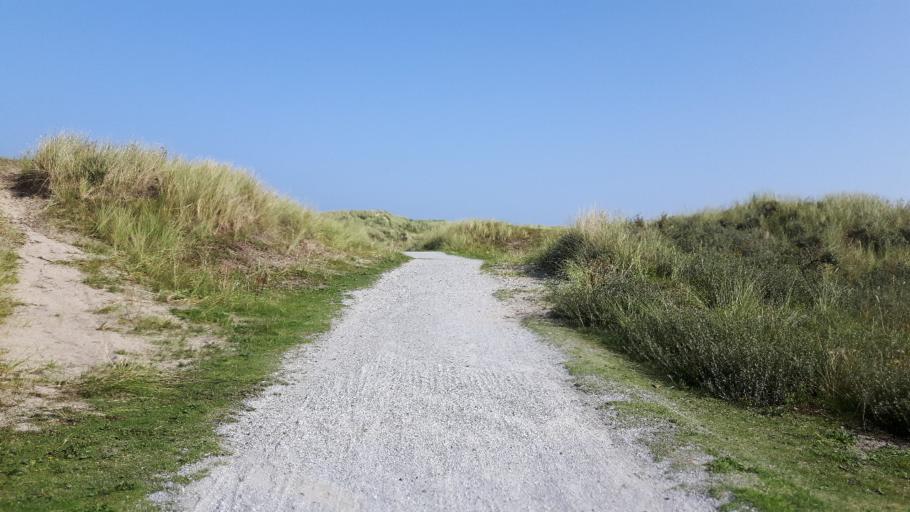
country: NL
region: Friesland
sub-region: Gemeente Ameland
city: Nes
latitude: 53.4602
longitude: 5.8166
